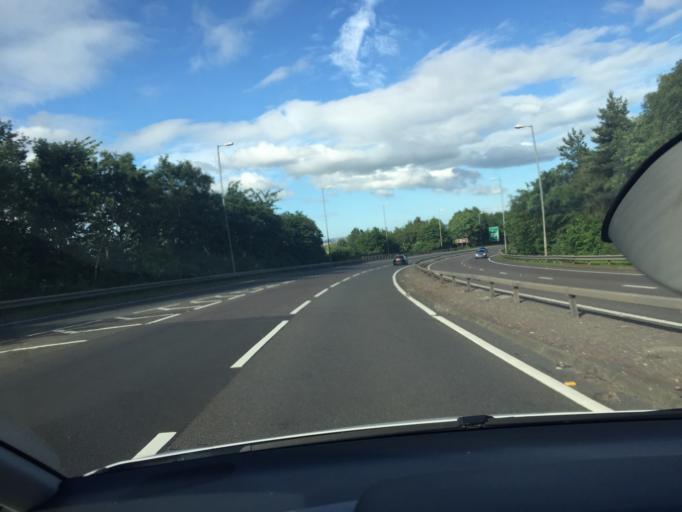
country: GB
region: Scotland
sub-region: South Lanarkshire
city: Bothwell
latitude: 55.7913
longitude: -4.0788
